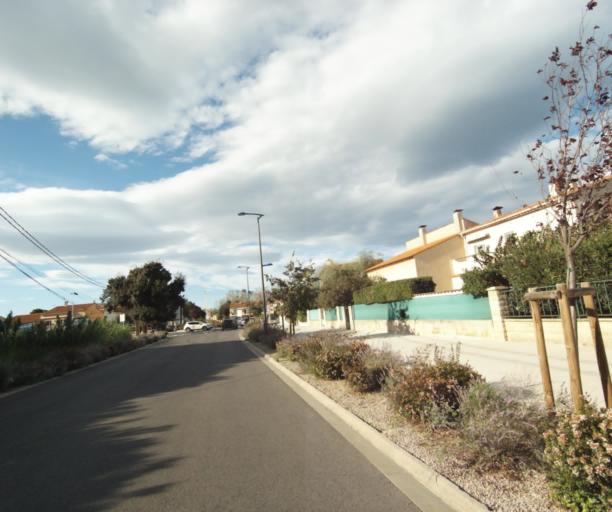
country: FR
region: Languedoc-Roussillon
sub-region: Departement des Pyrenees-Orientales
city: Argelers
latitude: 42.5465
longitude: 3.0342
